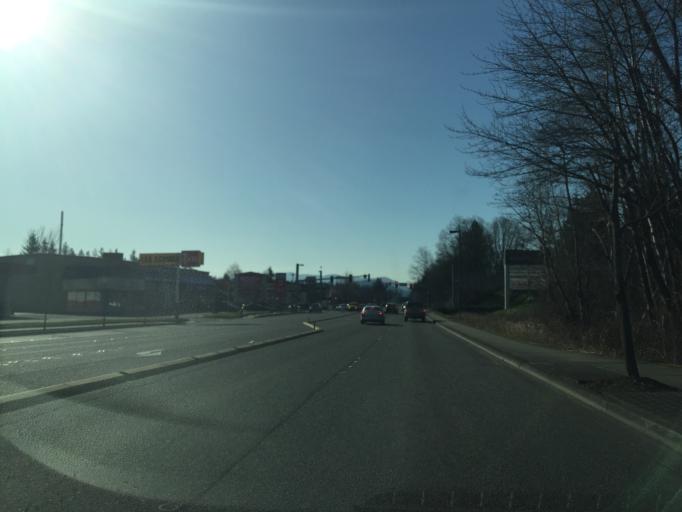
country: US
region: Washington
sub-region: Whatcom County
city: Bellingham
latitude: 48.7882
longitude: -122.4862
